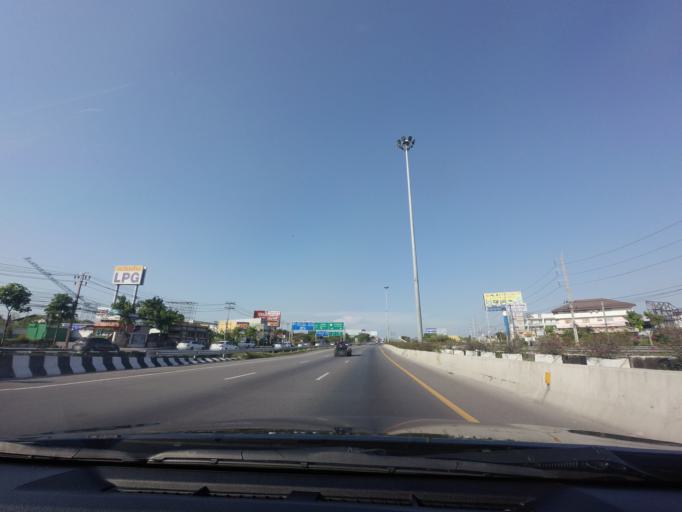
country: TH
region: Bangkok
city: Bang Bon
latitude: 13.6400
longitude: 100.4068
